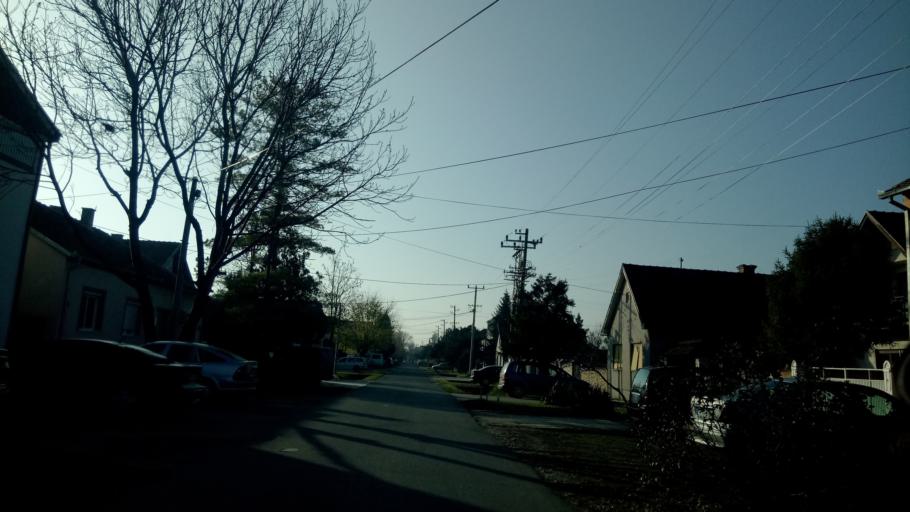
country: RS
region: Autonomna Pokrajina Vojvodina
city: Nova Pazova
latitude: 44.9420
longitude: 20.2138
